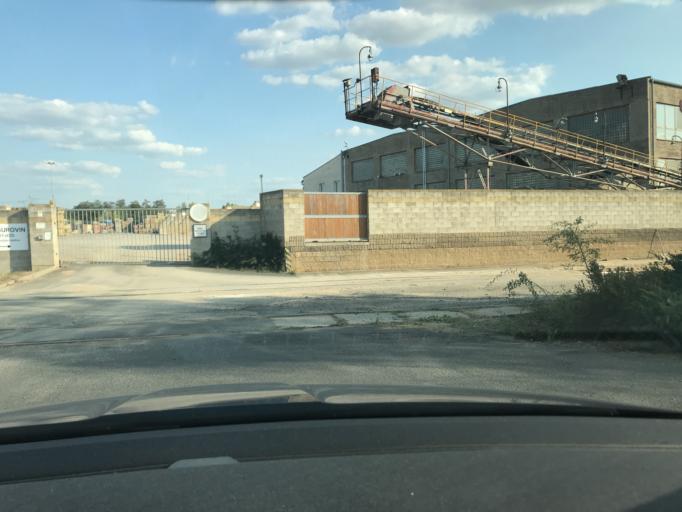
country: CZ
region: Ustecky
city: Postoloprty
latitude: 50.3604
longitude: 13.6823
